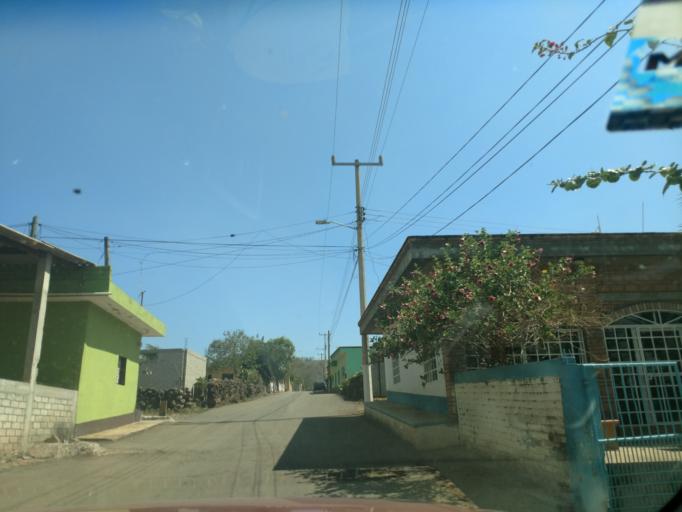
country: MX
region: Nayarit
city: Santa Maria del Oro
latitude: 21.4656
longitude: -104.6592
